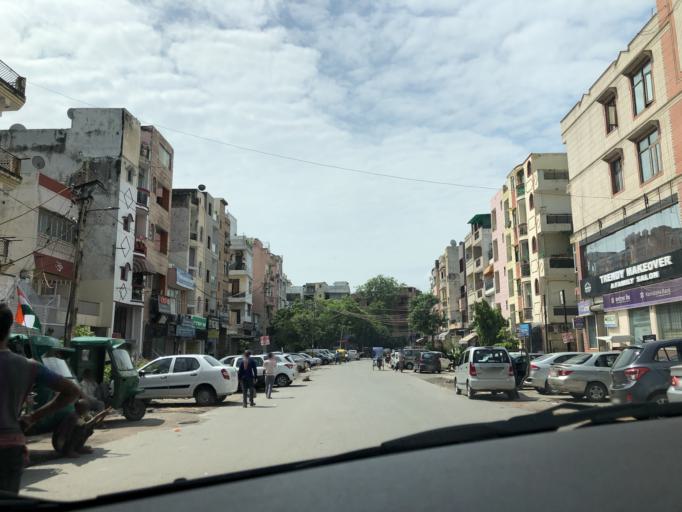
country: IN
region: NCT
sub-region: New Delhi
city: New Delhi
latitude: 28.5728
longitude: 77.2432
